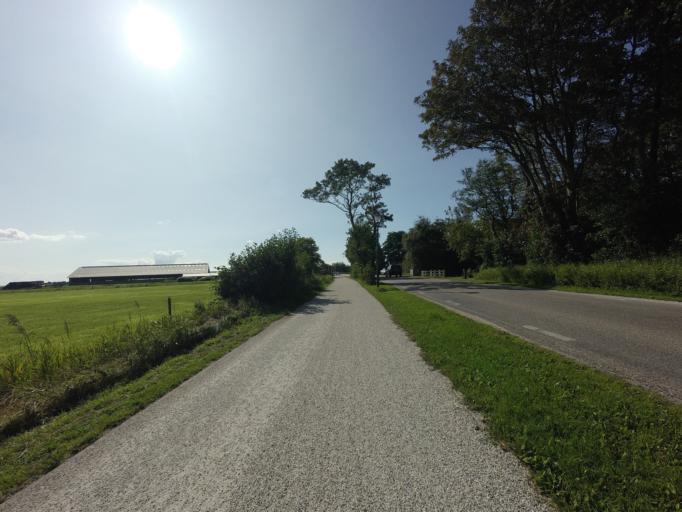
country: NL
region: Friesland
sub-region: Gemeente Terschelling
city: West-Terschelling
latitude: 53.3952
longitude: 5.3329
